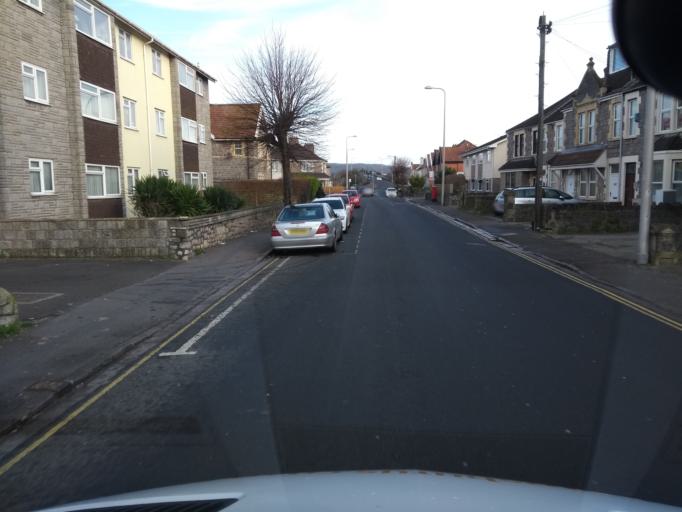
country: GB
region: England
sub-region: North Somerset
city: Weston-super-Mare
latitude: 51.3339
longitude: -2.9721
